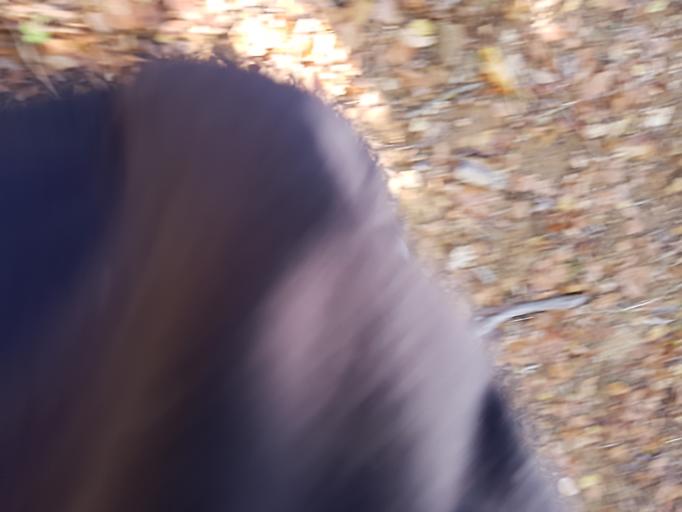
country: GR
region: Ionian Islands
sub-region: Nomos Kerkyras
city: Acharavi
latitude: 39.7458
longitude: 19.8824
